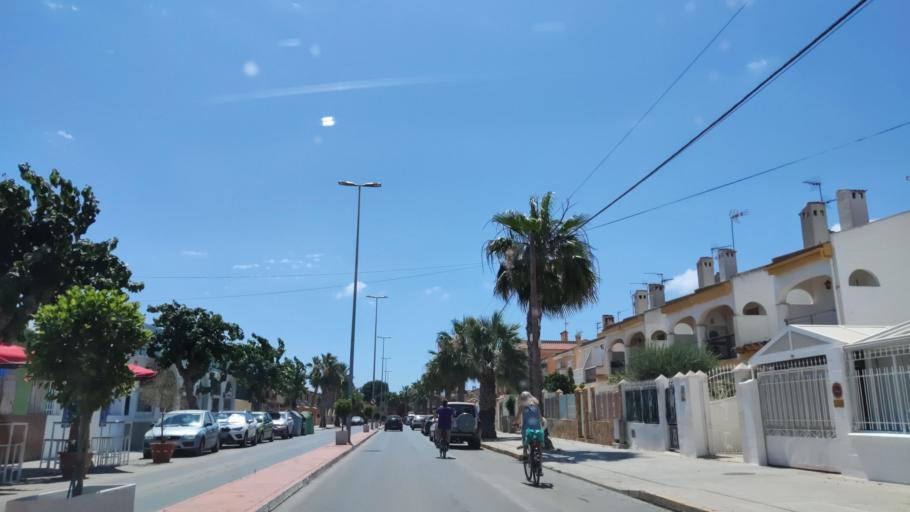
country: ES
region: Murcia
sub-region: Murcia
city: Los Alcazares
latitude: 37.7587
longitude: -0.8380
